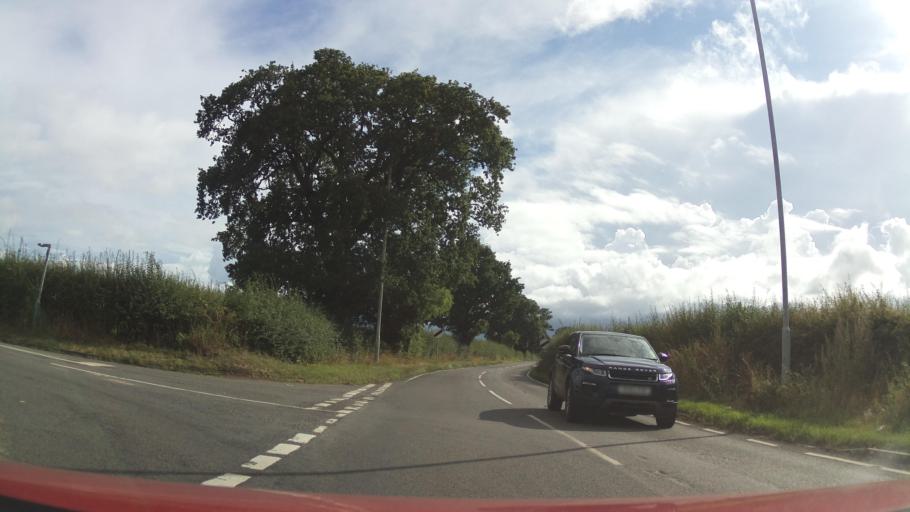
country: GB
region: England
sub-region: Telford and Wrekin
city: Madeley
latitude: 52.6388
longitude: -2.4131
